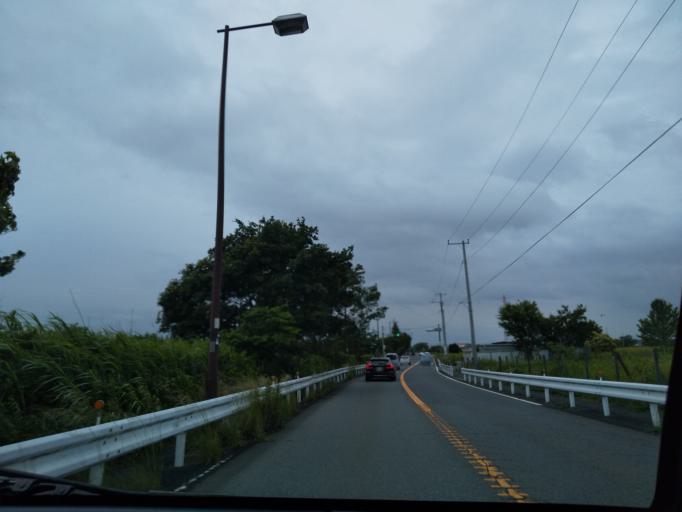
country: JP
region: Kanagawa
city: Fujisawa
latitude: 35.3973
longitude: 139.5044
